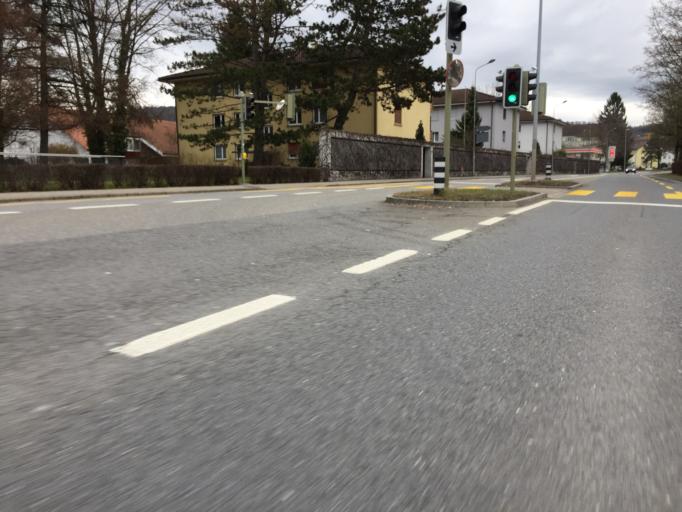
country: CH
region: Bern
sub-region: Emmental District
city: Burgdorf
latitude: 47.0635
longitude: 7.6145
